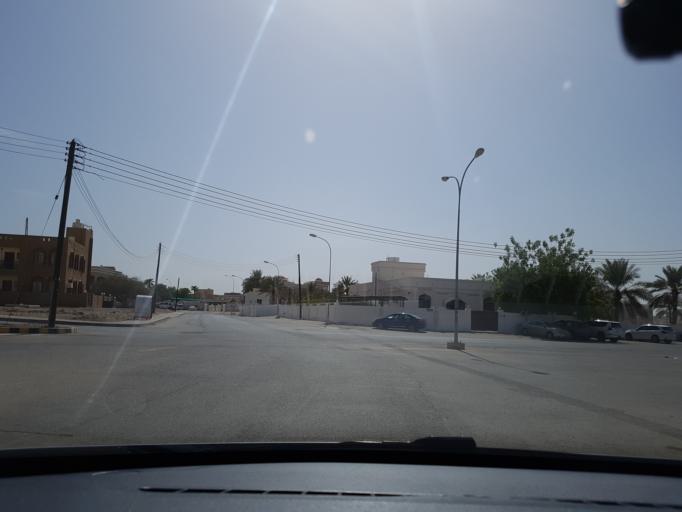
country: OM
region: Muhafazat Masqat
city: Bawshar
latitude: 23.5532
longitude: 58.4109
